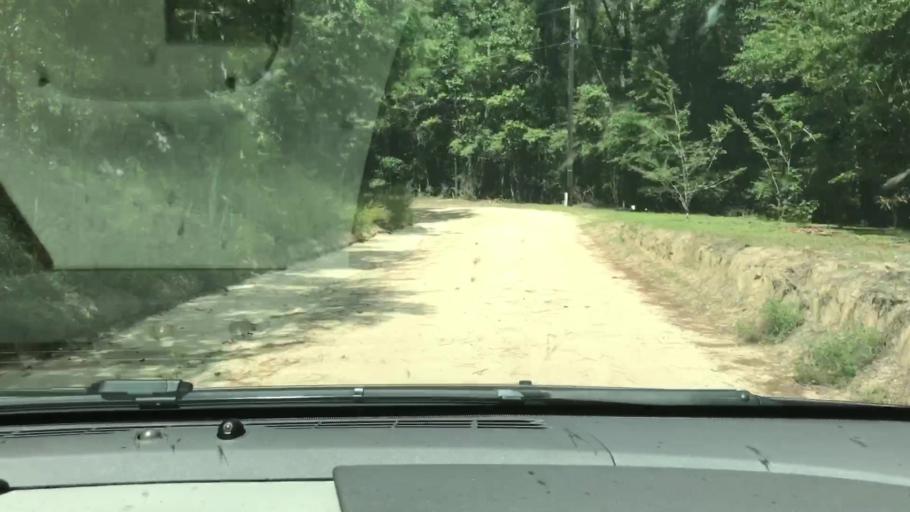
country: US
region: Georgia
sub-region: Clay County
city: Fort Gaines
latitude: 31.7325
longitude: -85.0882
